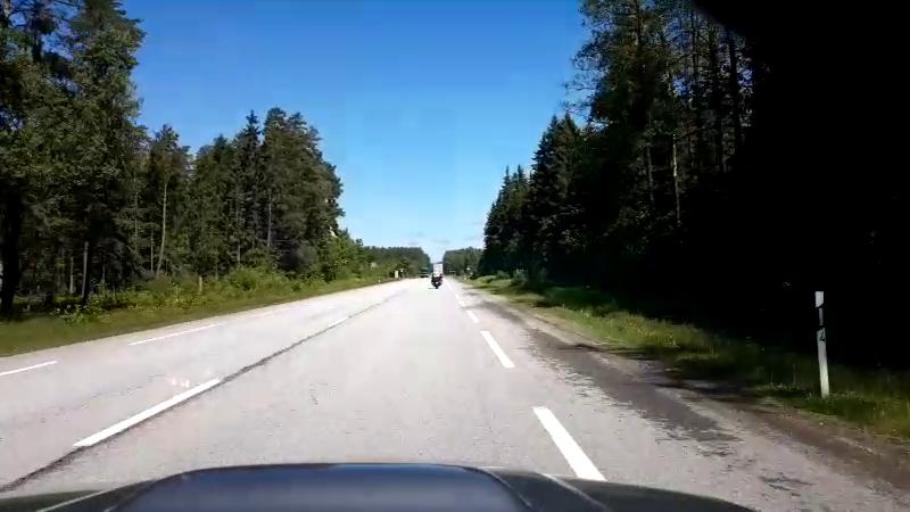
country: LV
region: Saulkrastu
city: Saulkrasti
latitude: 57.4243
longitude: 24.4291
